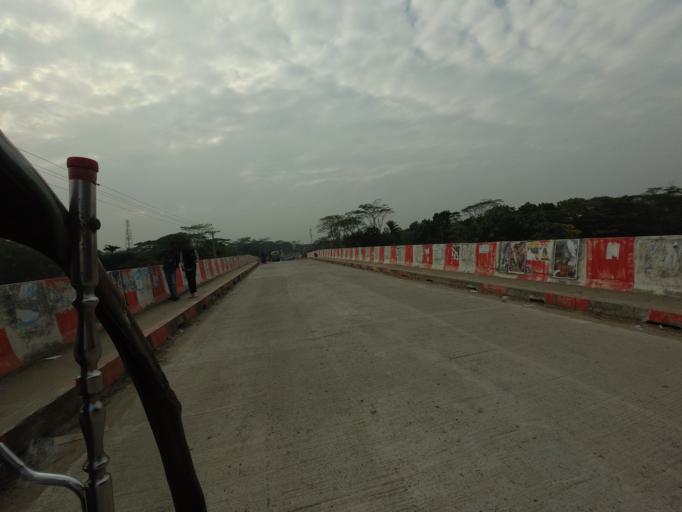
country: BD
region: Barisal
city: Nalchiti
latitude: 22.4539
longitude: 90.3435
